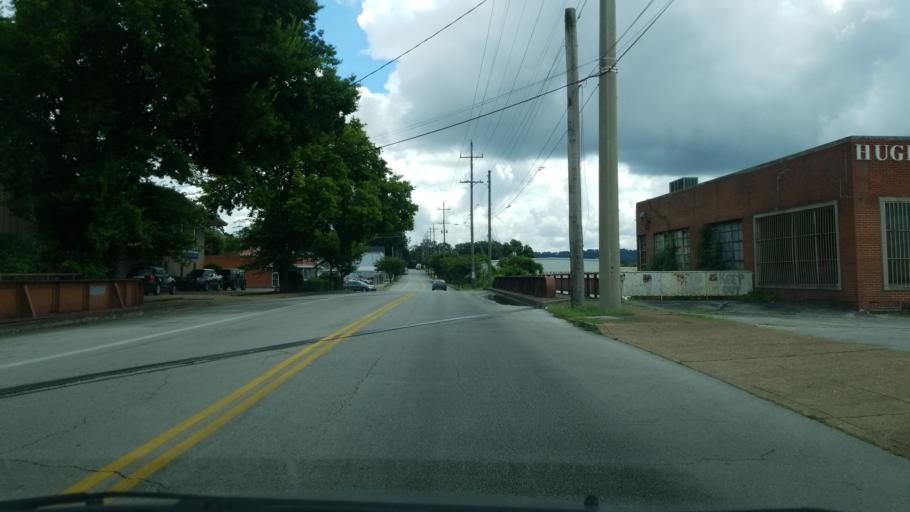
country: US
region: Tennessee
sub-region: Hamilton County
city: Chattanooga
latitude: 35.0397
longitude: -85.2985
